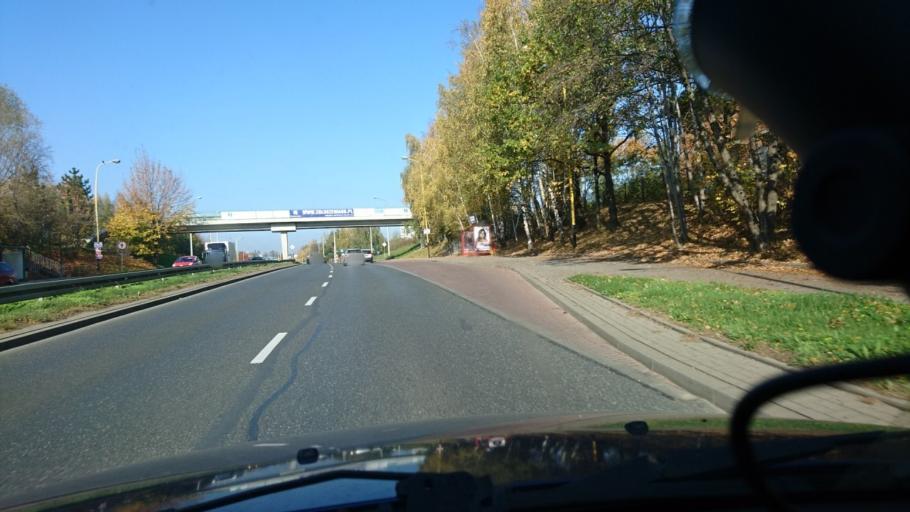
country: PL
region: Silesian Voivodeship
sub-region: Bielsko-Biala
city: Bielsko-Biala
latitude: 49.8081
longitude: 19.0291
